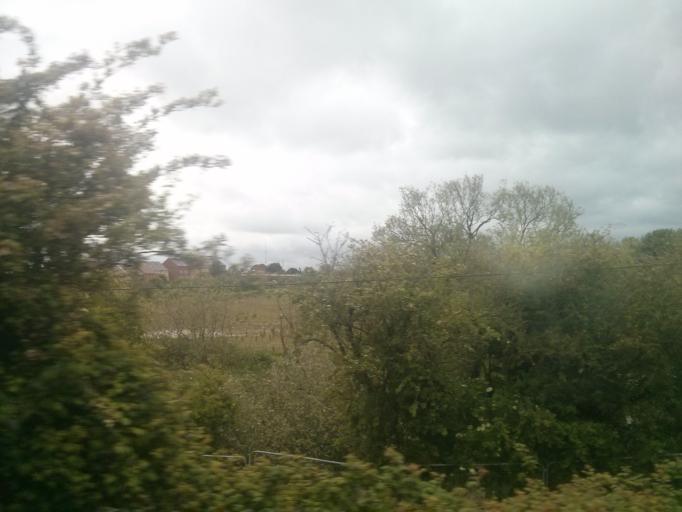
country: GB
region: England
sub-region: Wiltshire
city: Westbury
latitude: 51.2712
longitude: -2.1922
